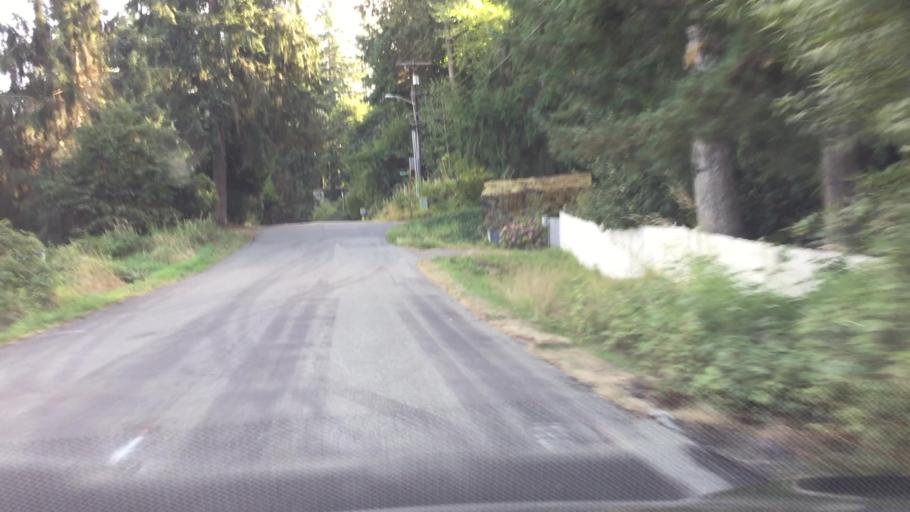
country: US
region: Washington
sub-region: King County
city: Cottage Lake
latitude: 47.7576
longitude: -122.0923
